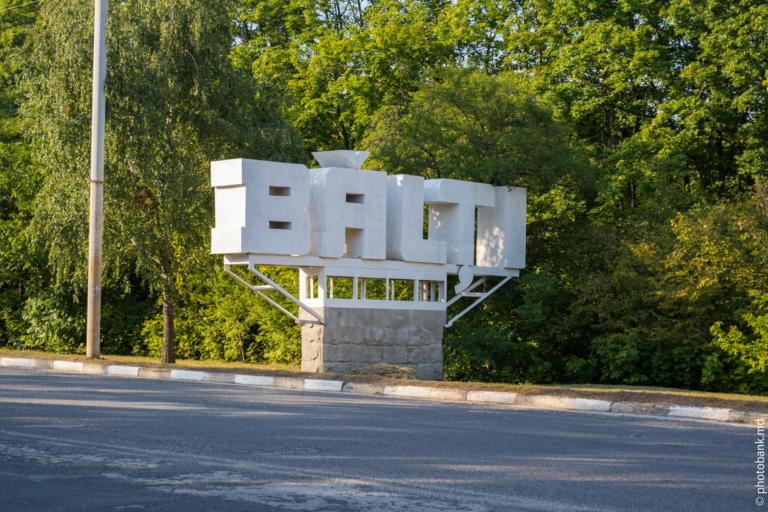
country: MD
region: Balti
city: Balti
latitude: 47.7433
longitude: 27.9545
